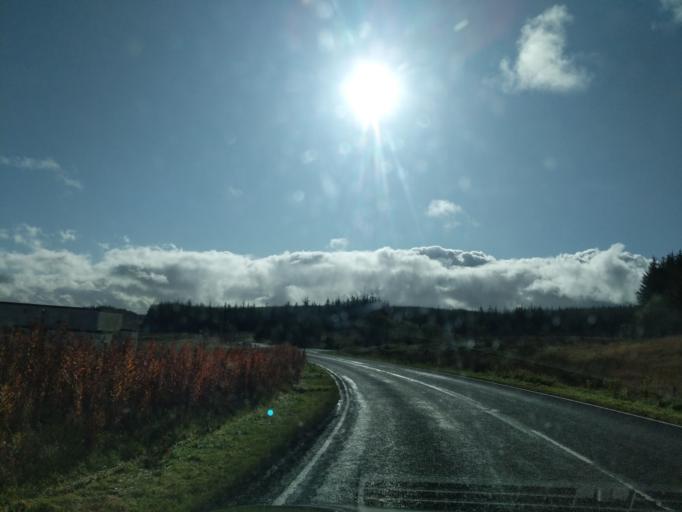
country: GB
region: Scotland
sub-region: Dumfries and Galloway
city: Moffat
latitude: 55.3874
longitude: -3.4863
